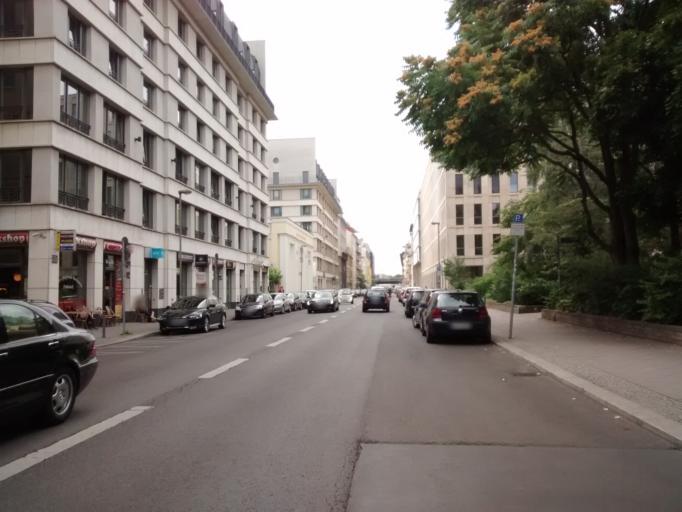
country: DE
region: Berlin
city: Tiergarten Bezirk
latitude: 52.5232
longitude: 13.3832
